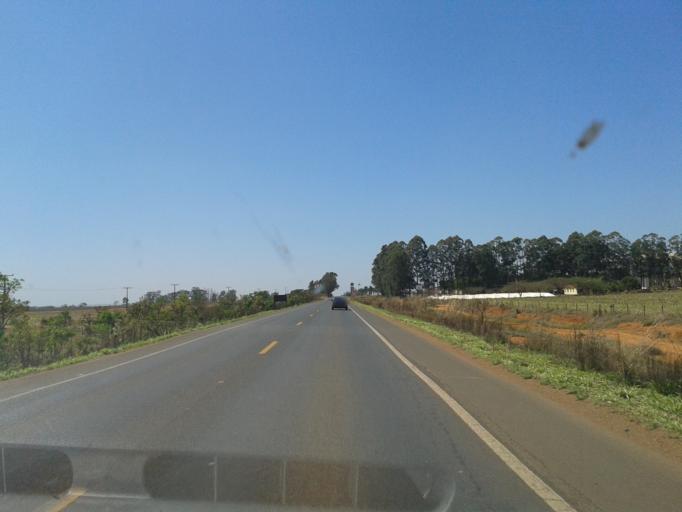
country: BR
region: Minas Gerais
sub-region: Uberaba
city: Uberaba
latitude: -19.3109
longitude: -47.5764
